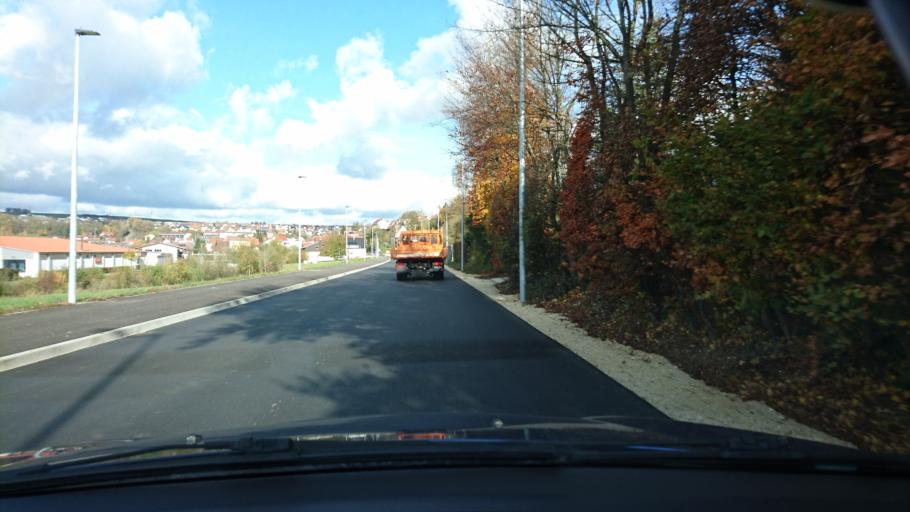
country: DE
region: Baden-Wuerttemberg
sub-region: Regierungsbezirk Stuttgart
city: Huttlingen
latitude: 48.8853
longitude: 10.0990
